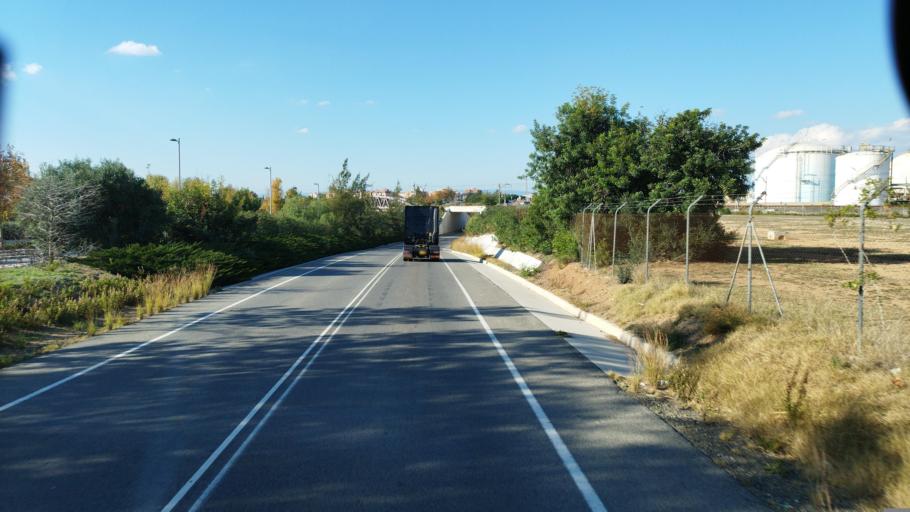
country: ES
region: Catalonia
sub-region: Provincia de Tarragona
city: Vila-seca
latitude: 41.1020
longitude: 1.1621
